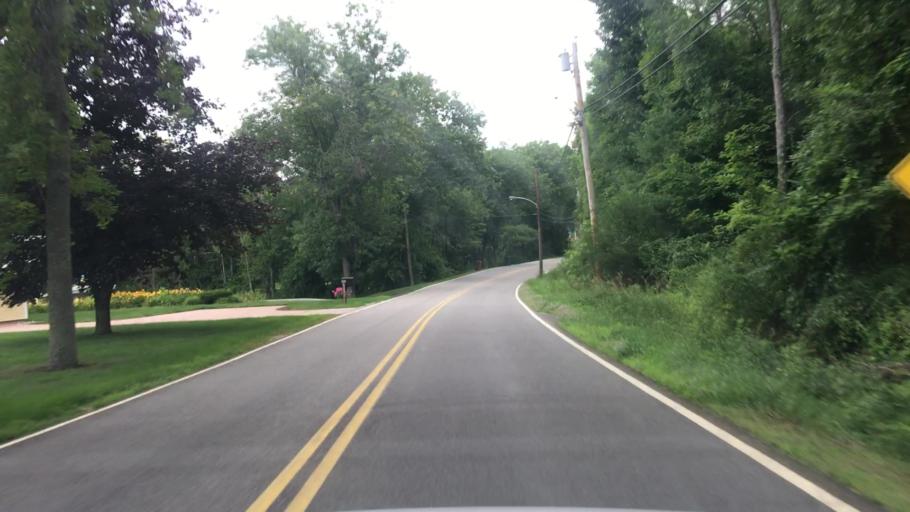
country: US
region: Maine
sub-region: York County
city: Dayton
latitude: 43.5339
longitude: -70.5157
